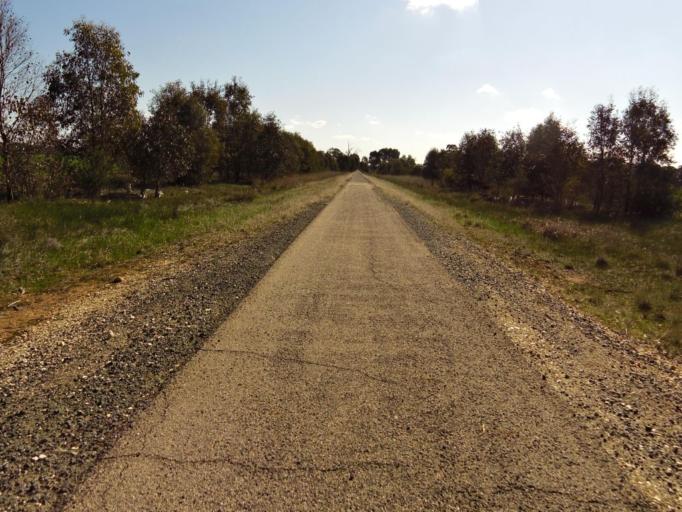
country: AU
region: New South Wales
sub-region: Corowa Shire
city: Corowa
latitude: -36.0220
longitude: 146.4250
